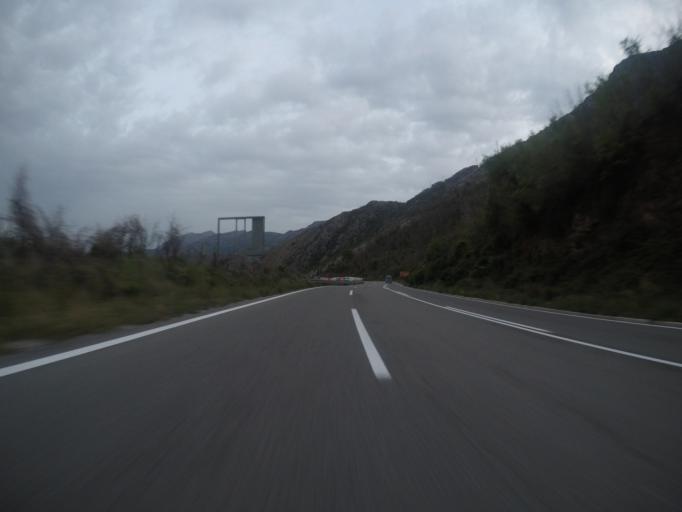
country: ME
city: Petrovac na Moru
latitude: 42.1790
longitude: 18.9963
